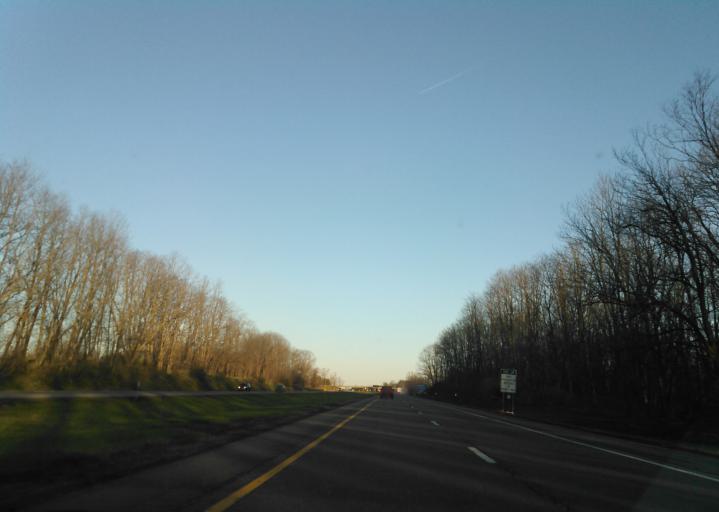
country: US
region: New York
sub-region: Monroe County
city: Pittsford
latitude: 43.0263
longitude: -77.5055
